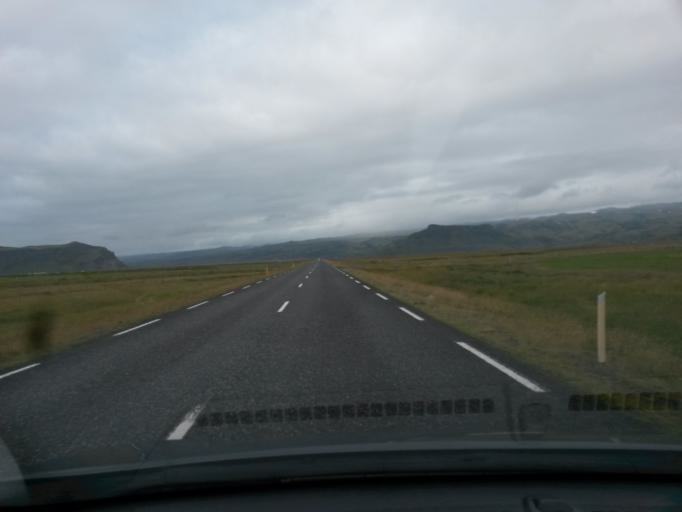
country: IS
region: South
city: Vestmannaeyjar
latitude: 63.4399
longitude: -19.1966
